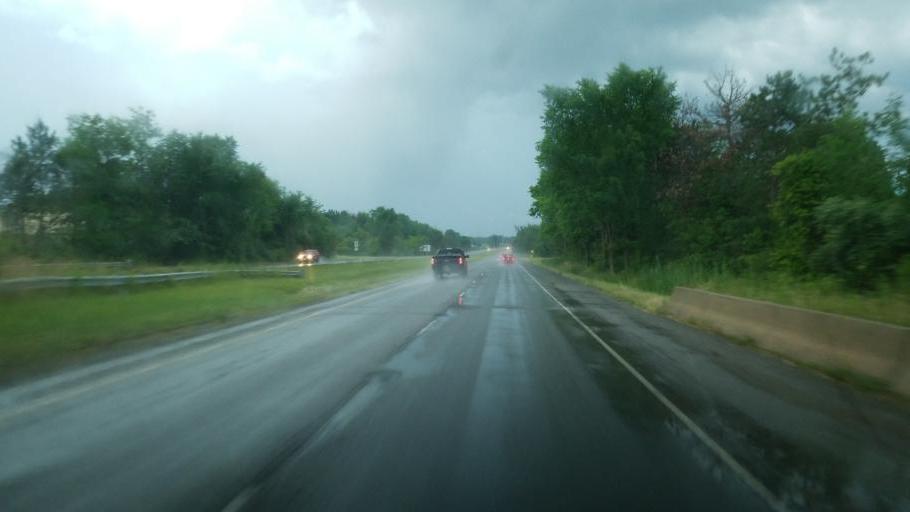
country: US
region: Ohio
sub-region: Summit County
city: Norton
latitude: 41.0498
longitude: -81.6625
